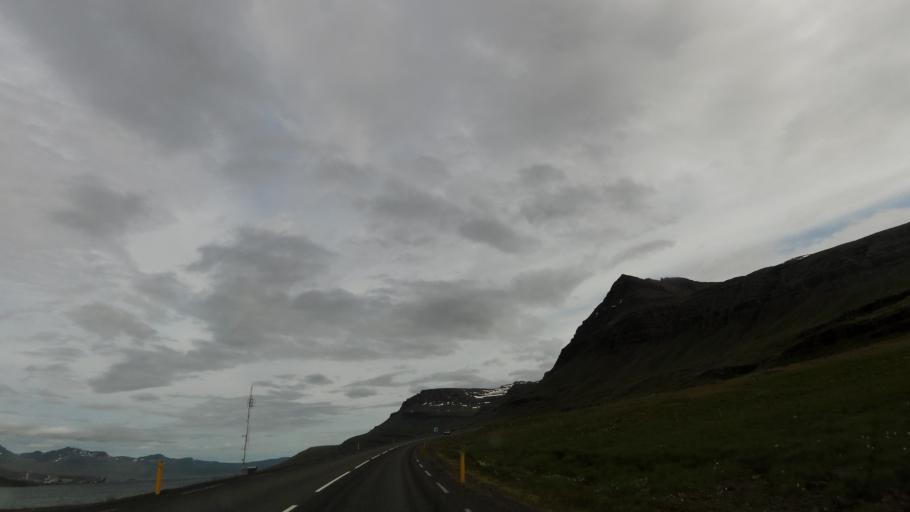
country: IS
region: East
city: Reydarfjoerdur
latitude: 65.0162
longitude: -14.2114
